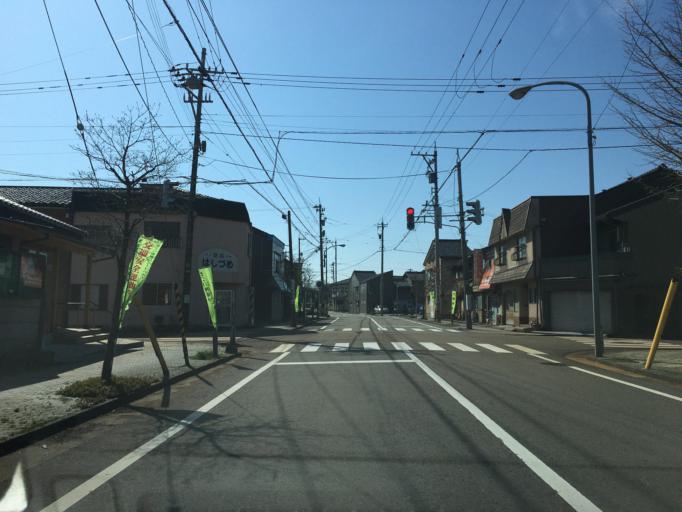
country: JP
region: Toyama
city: Nishishinminato
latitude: 36.7790
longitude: 137.0933
